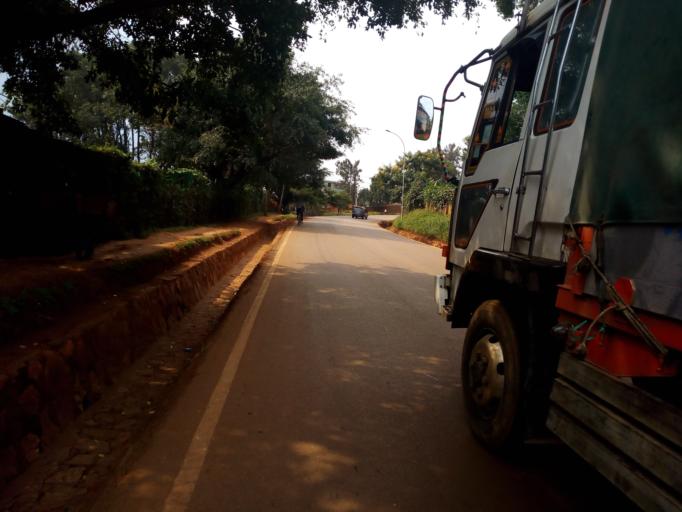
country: UG
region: Central Region
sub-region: Wakiso District
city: Kireka
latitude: 0.3256
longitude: 32.6231
